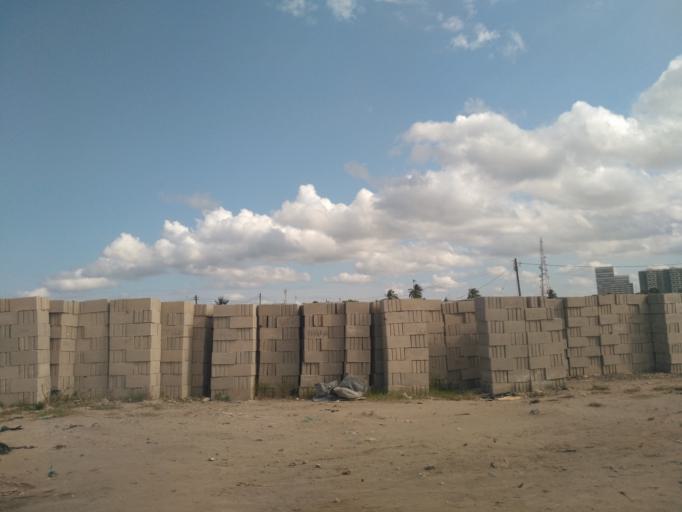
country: TZ
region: Dar es Salaam
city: Magomeni
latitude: -6.7666
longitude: 39.2644
